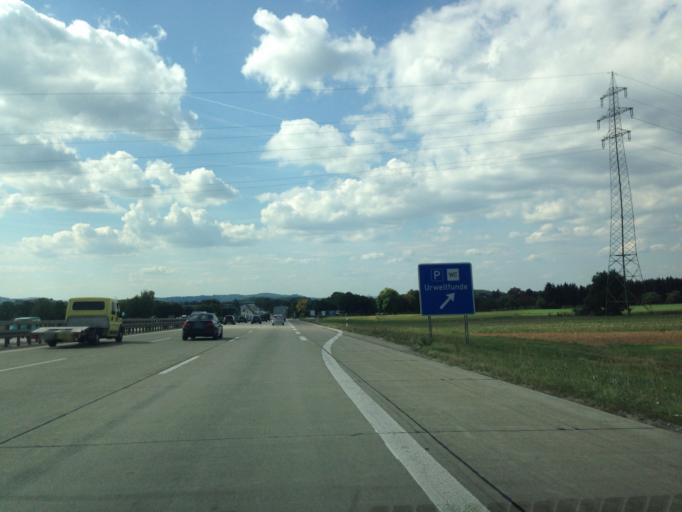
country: DE
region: Baden-Wuerttemberg
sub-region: Regierungsbezirk Stuttgart
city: Weilheim an der Teck
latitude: 48.6326
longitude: 9.5433
